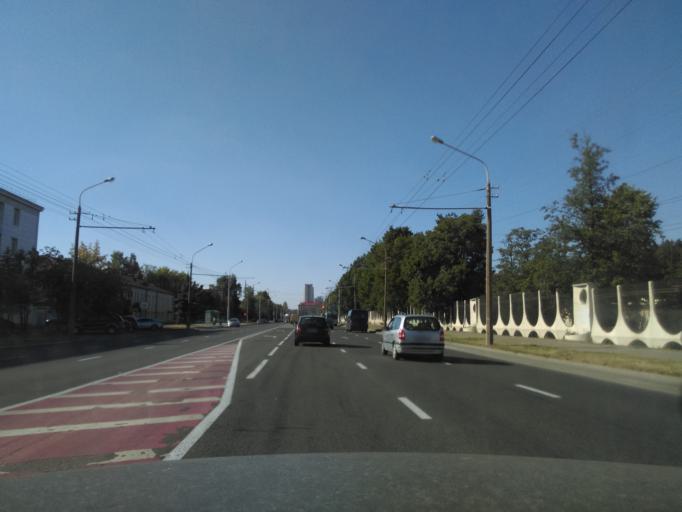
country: BY
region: Minsk
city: Minsk
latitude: 53.9092
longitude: 27.6110
